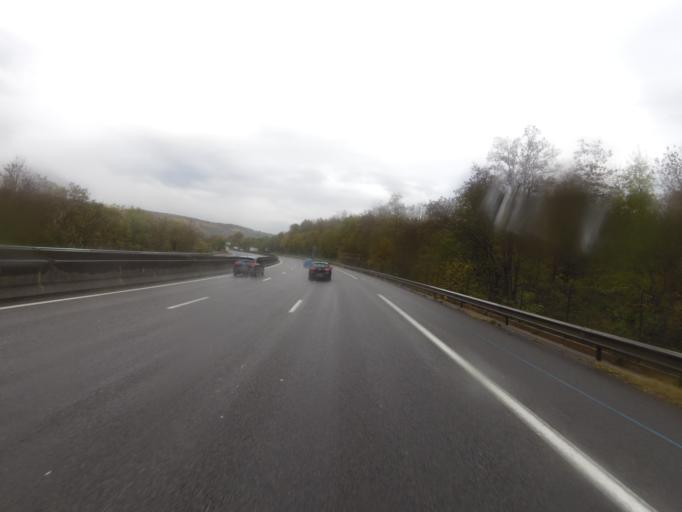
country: FR
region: Rhone-Alpes
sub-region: Departement de l'Isere
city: Reventin-Vaugris
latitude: 45.4839
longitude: 4.8348
